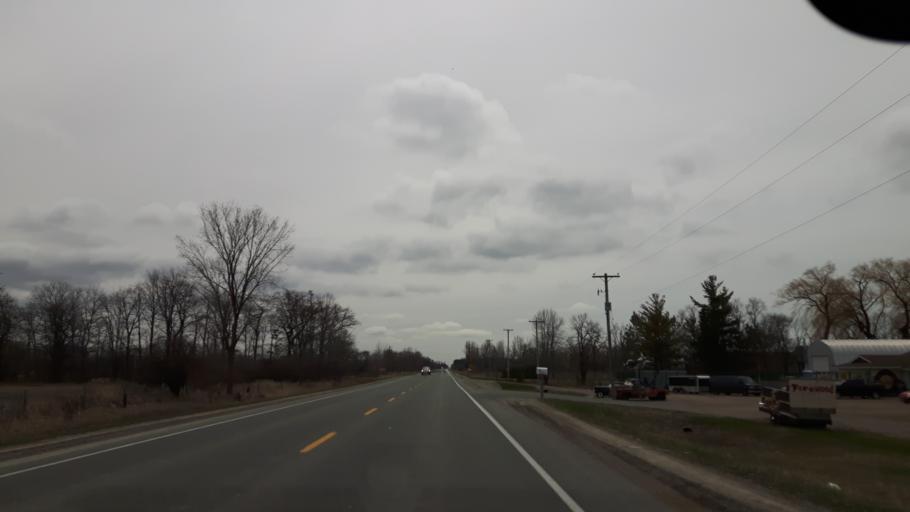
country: CA
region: Ontario
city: Goderich
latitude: 43.7205
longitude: -81.7058
